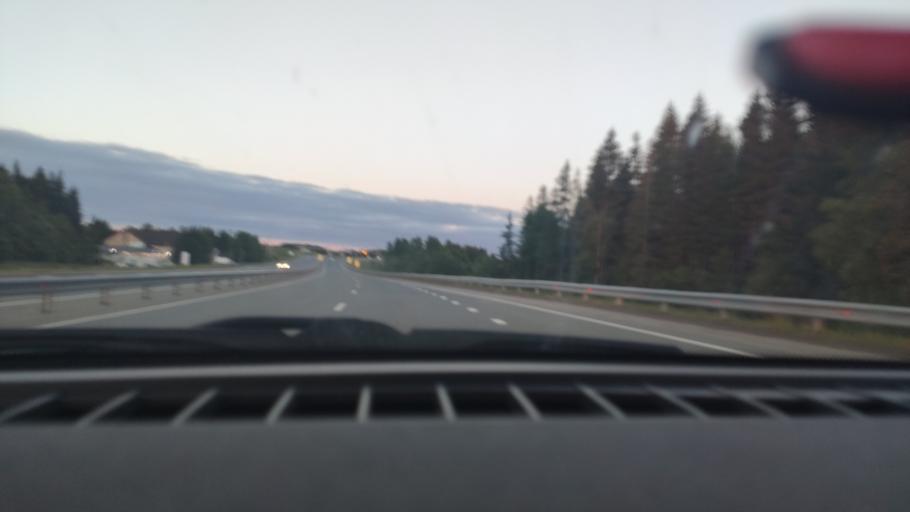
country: RU
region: Perm
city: Polazna
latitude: 58.2723
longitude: 56.4154
